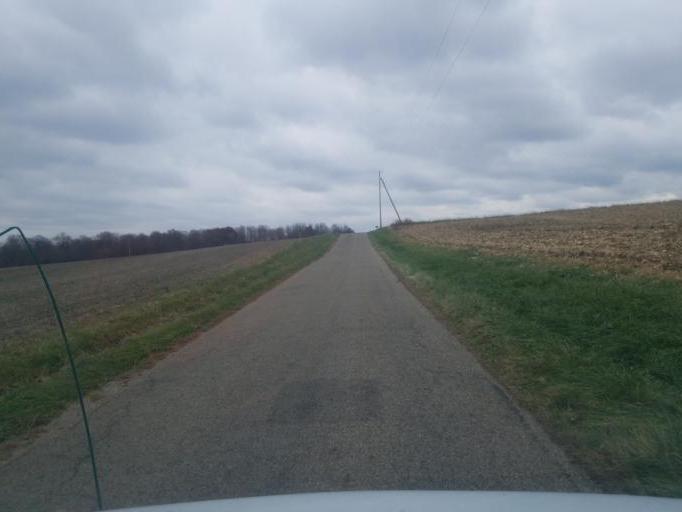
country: US
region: Ohio
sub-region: Knox County
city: Fredericktown
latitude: 40.4741
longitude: -82.5109
